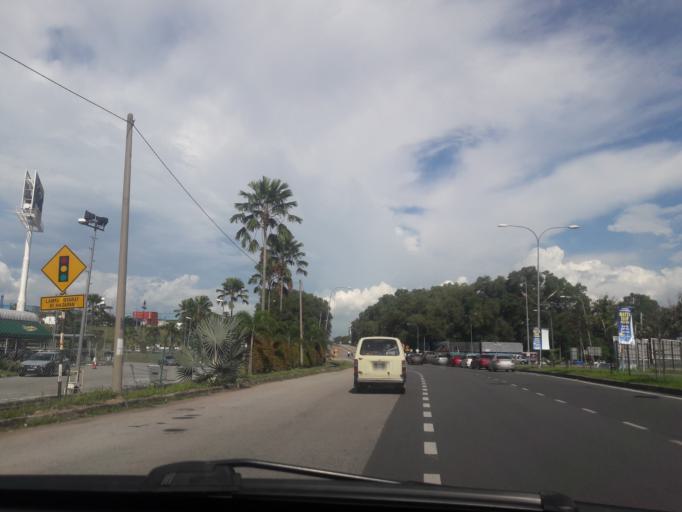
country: MY
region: Kedah
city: Sungai Petani
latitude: 5.6153
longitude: 100.4718
